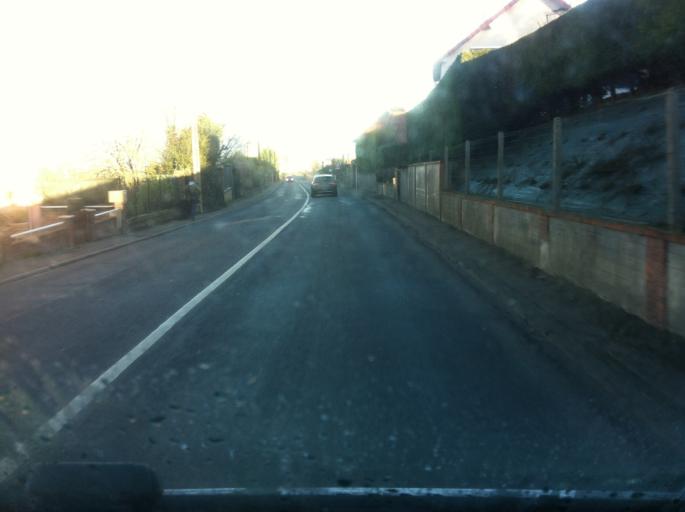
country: FR
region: Haute-Normandie
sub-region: Departement de la Seine-Maritime
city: Le Treport
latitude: 50.0556
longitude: 1.3727
